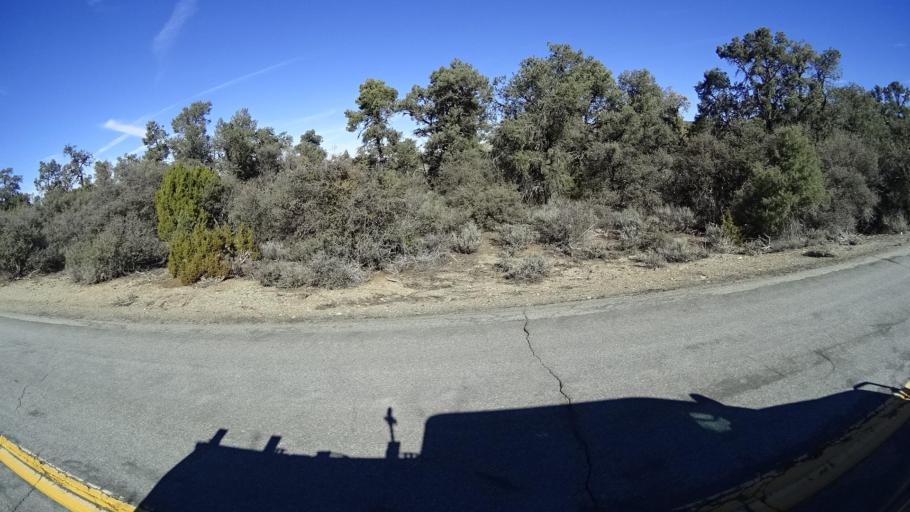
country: US
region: California
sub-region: Kern County
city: Pine Mountain Club
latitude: 34.8751
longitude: -119.2878
